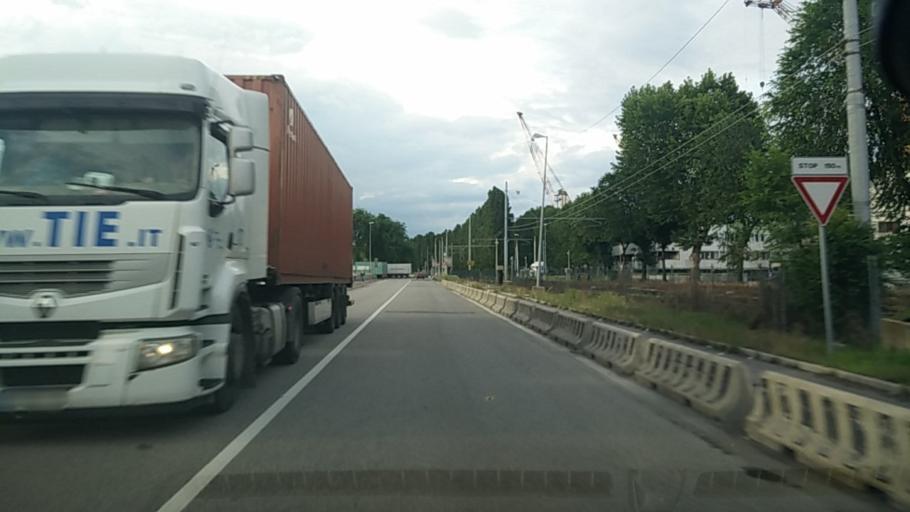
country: IT
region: Veneto
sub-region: Provincia di Venezia
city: Mestre
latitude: 45.4729
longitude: 12.2386
